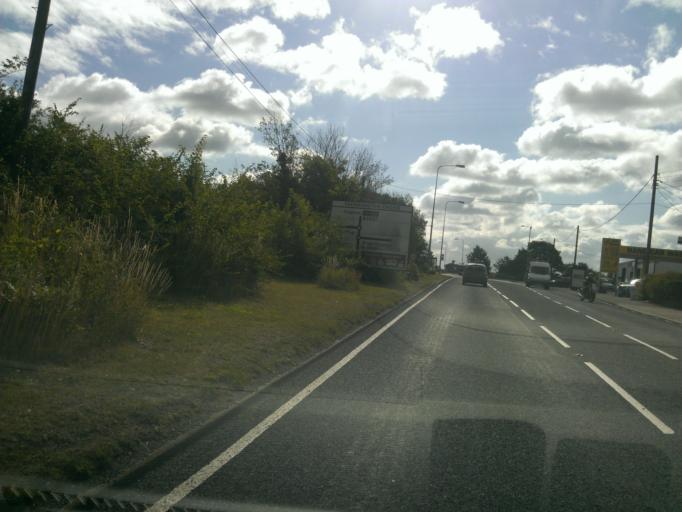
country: GB
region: England
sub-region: Essex
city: Alresford
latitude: 51.8428
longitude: 1.0267
